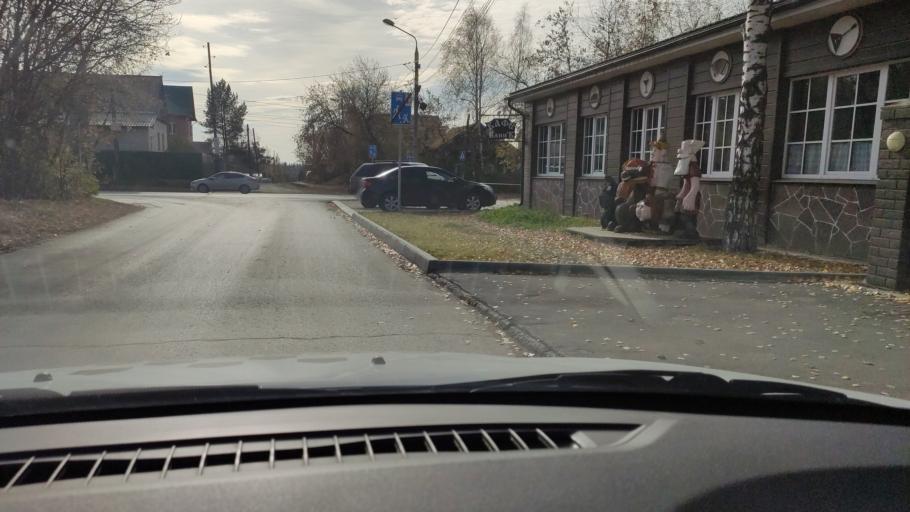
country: RU
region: Perm
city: Kondratovo
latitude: 58.0410
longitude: 56.1182
